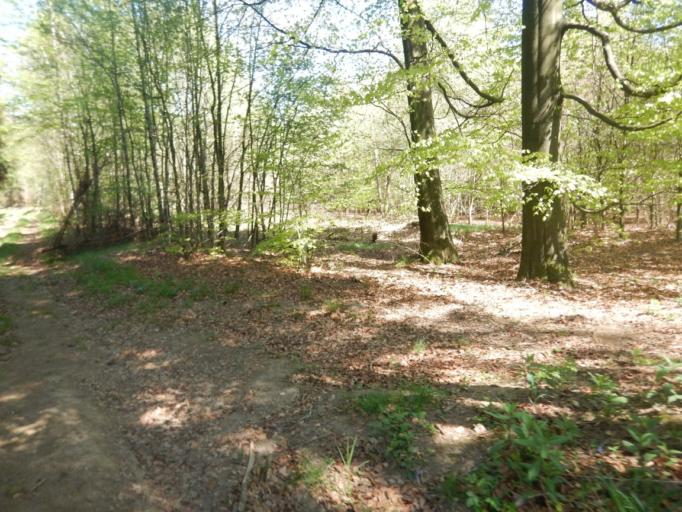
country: LU
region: Diekirch
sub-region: Canton de Clervaux
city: Weiswampach
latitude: 50.1553
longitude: 6.0426
